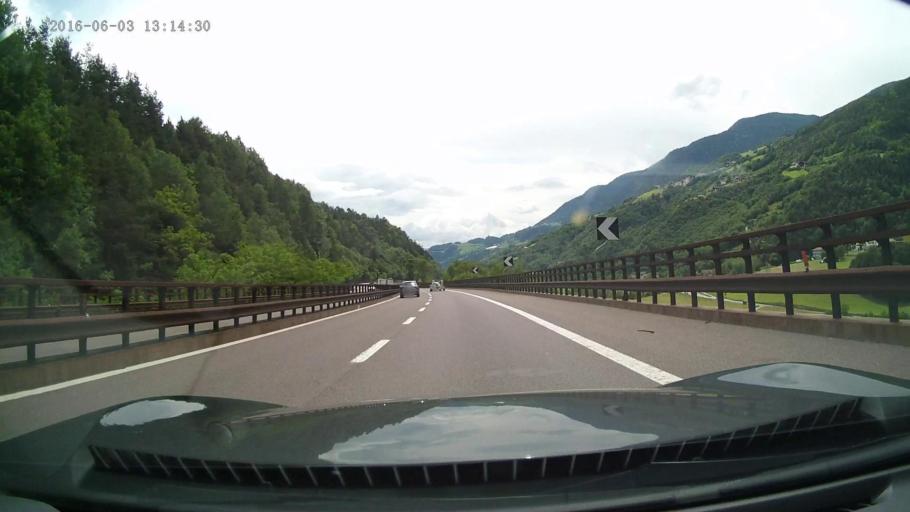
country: IT
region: Trentino-Alto Adige
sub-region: Bolzano
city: Villandro
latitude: 46.6172
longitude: 11.5409
